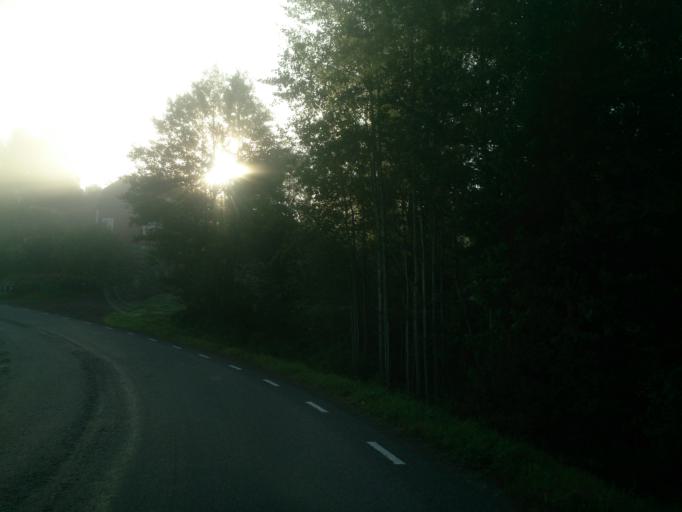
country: SE
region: OEstergoetland
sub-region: Atvidabergs Kommun
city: Atvidaberg
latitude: 58.1824
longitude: 16.0476
